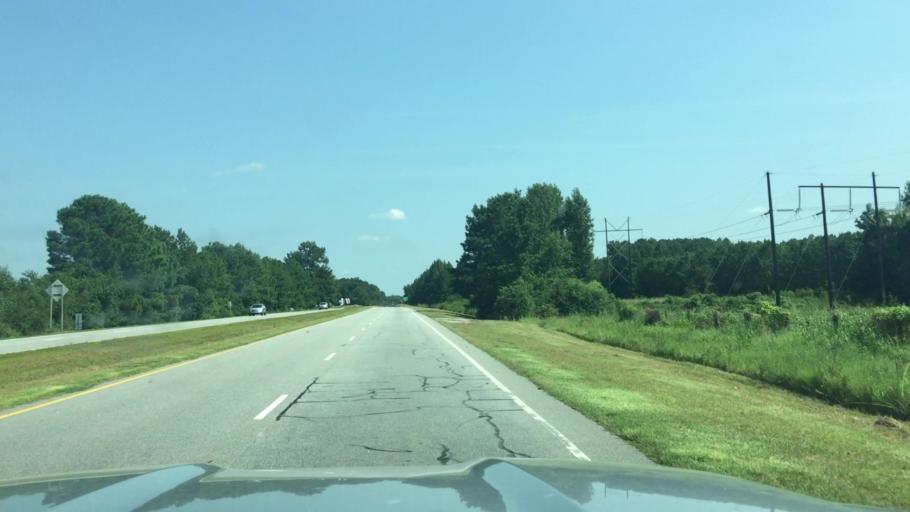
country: US
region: North Carolina
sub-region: Martin County
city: Williamston
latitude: 35.8118
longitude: -76.9131
